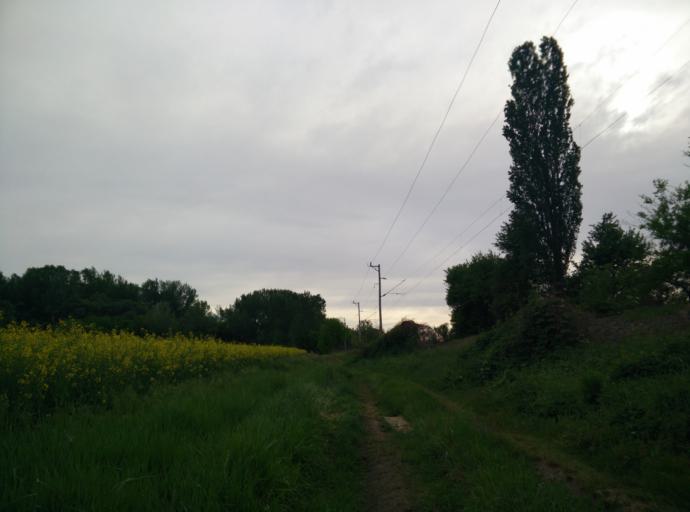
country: HU
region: Pest
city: Fot
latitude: 47.6064
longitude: 19.1609
